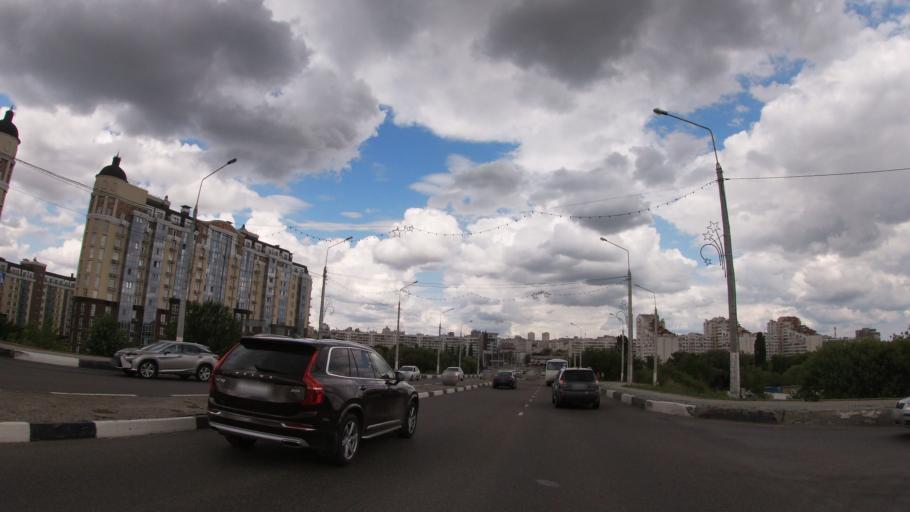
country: RU
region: Belgorod
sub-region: Belgorodskiy Rayon
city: Belgorod
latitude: 50.5882
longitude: 36.5887
